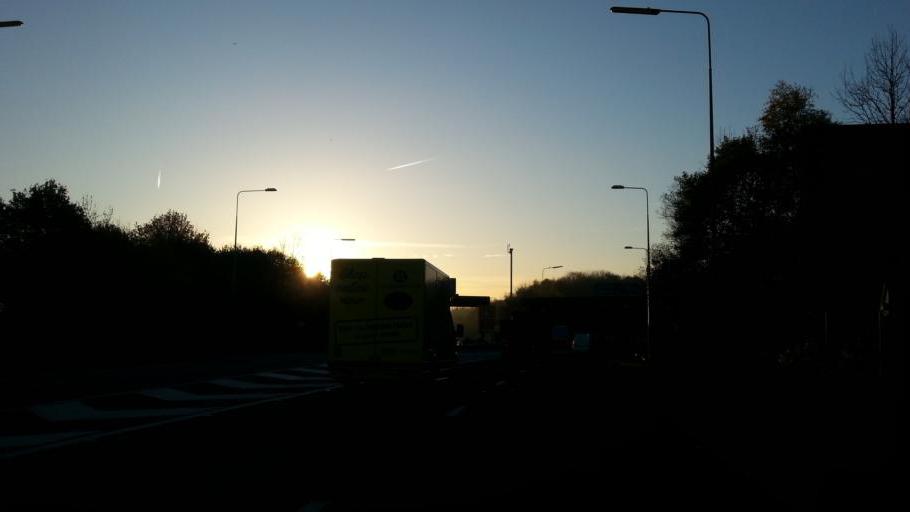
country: GB
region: England
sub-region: Hertfordshire
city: Abbots Langley
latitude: 51.7192
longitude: -0.3851
